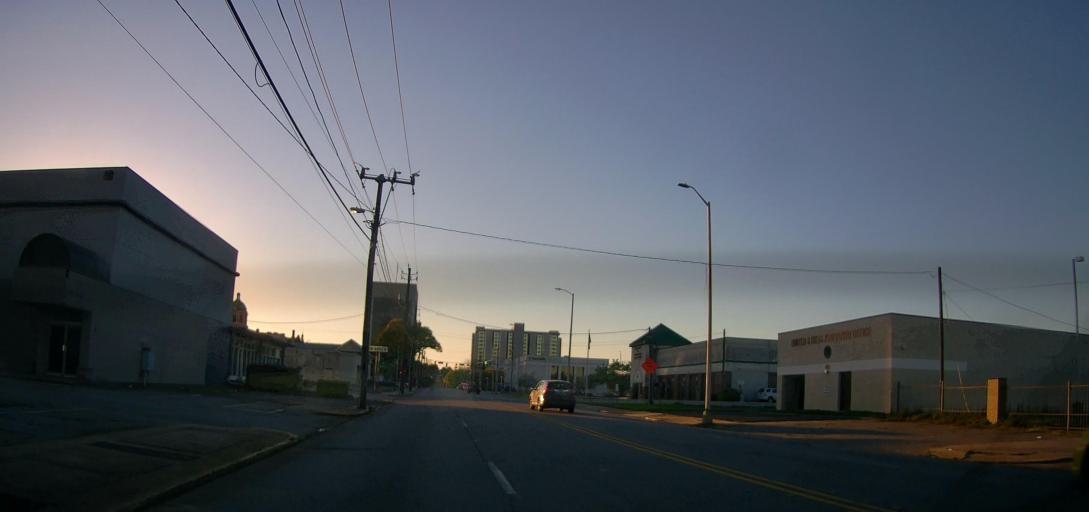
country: US
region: Georgia
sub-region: Bibb County
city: Macon
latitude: 32.8375
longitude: -83.6240
